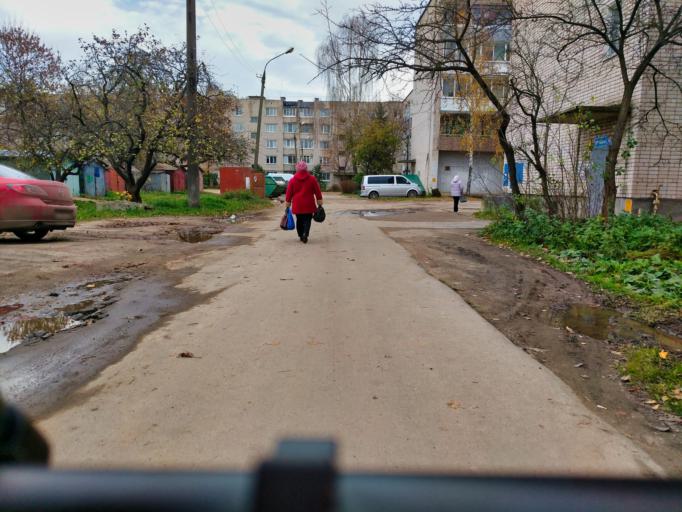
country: RU
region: Tverskaya
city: Rzhev
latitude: 56.2472
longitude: 34.3322
